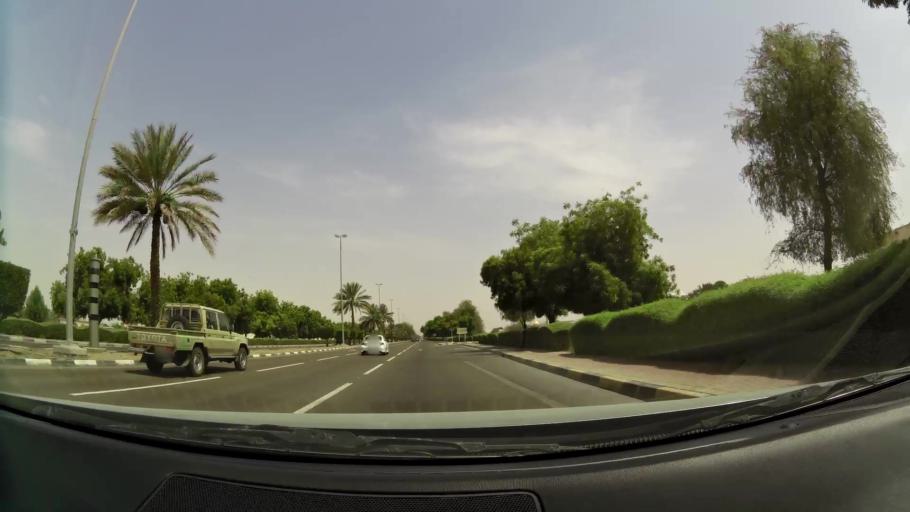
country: AE
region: Abu Dhabi
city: Al Ain
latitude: 24.1729
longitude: 55.7084
